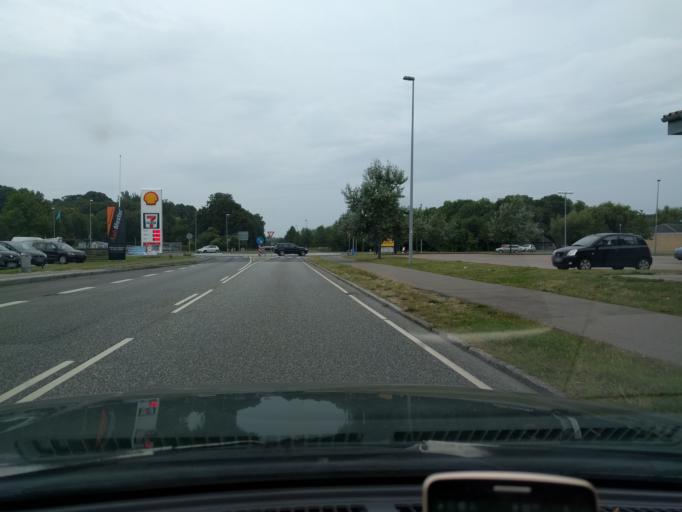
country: DK
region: Zealand
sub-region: Slagelse Kommune
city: Korsor
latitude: 55.3485
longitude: 11.1415
